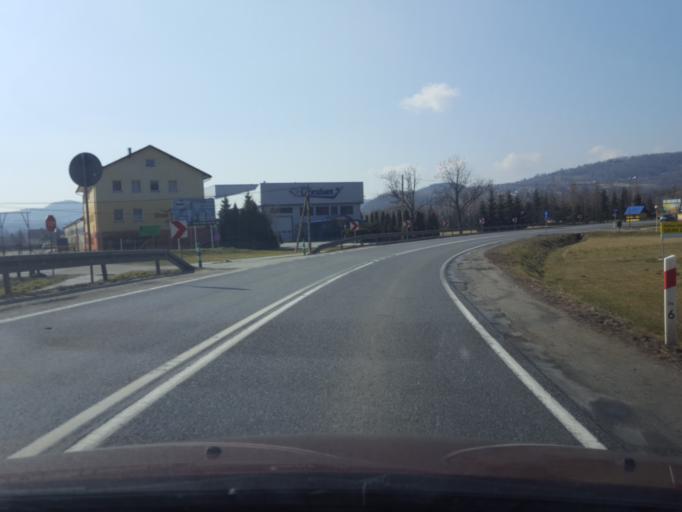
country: PL
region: Lesser Poland Voivodeship
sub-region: Powiat brzeski
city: Czchow
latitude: 49.8462
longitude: 20.6853
